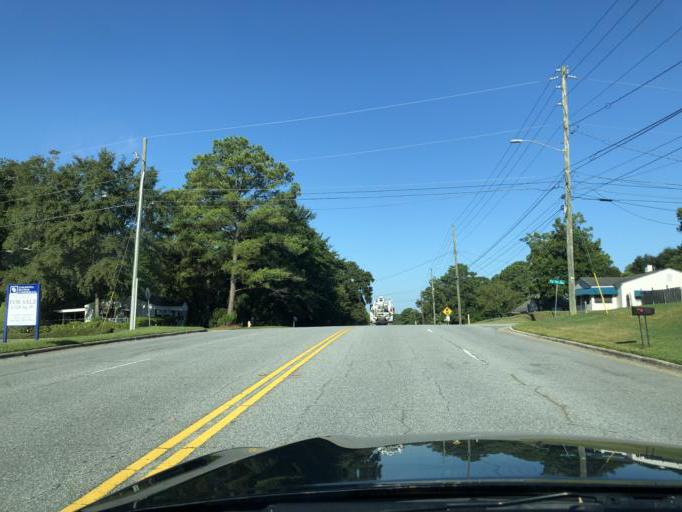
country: US
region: Georgia
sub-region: Muscogee County
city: Columbus
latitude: 32.4907
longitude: -84.9347
